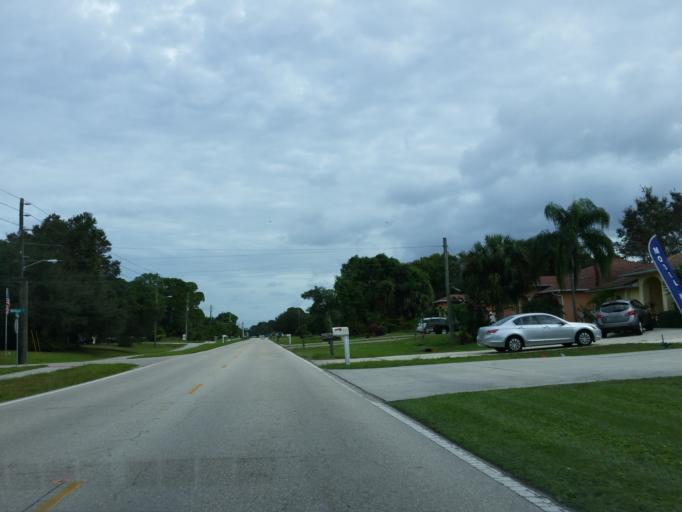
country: US
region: Florida
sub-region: Sarasota County
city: North Port
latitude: 27.0693
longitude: -82.2025
